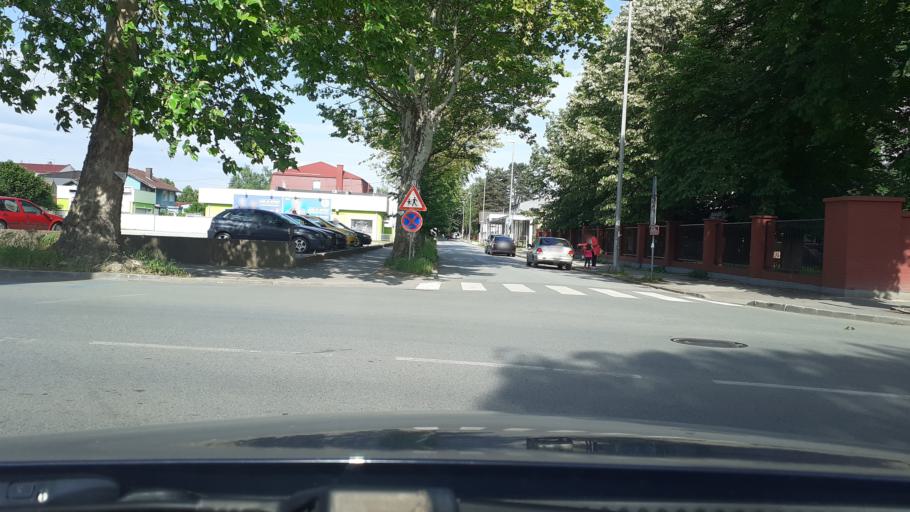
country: HR
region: Brodsko-Posavska
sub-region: Grad Slavonski Brod
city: Slavonski Brod
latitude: 45.1562
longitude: 18.0243
